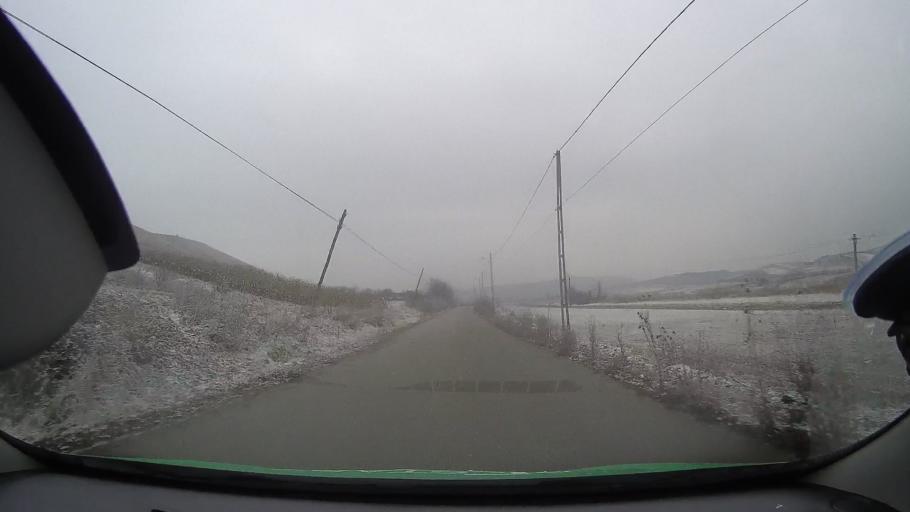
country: RO
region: Alba
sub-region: Comuna Noslac
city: Noslac
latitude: 46.3419
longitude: 23.9458
